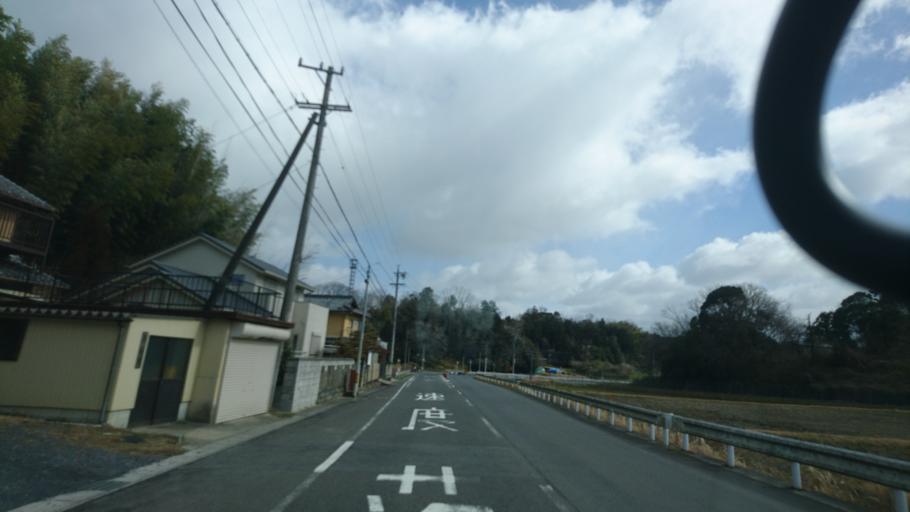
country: JP
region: Mie
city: Ueno-ebisumachi
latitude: 34.7281
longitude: 136.0730
